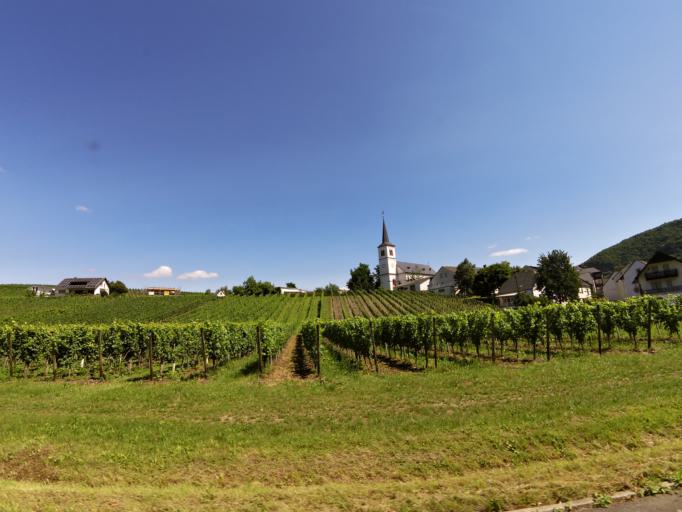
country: DE
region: Rheinland-Pfalz
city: Minheim
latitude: 49.8641
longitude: 6.9320
